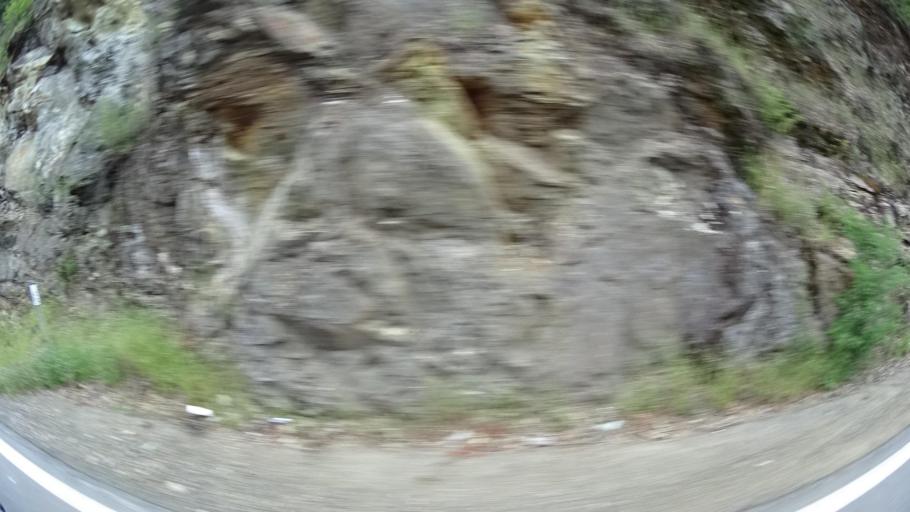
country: US
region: California
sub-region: Humboldt County
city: Willow Creek
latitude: 41.1149
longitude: -123.6879
